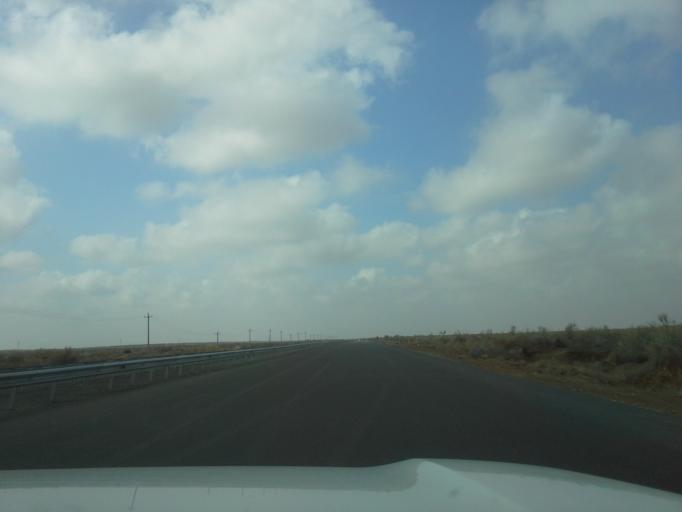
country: TM
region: Mary
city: Mary
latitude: 37.4076
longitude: 61.5334
